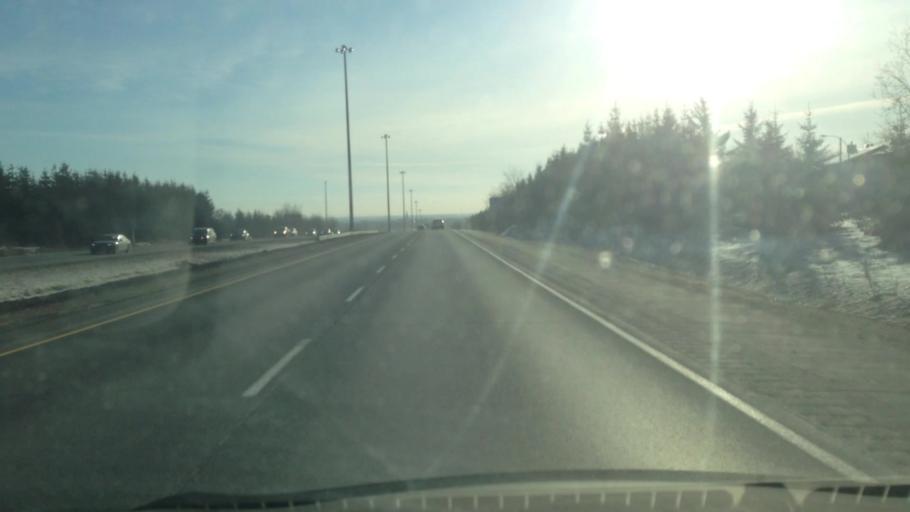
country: CA
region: Quebec
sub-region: Laurentides
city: Saint-Jerome
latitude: 45.8053
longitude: -74.0372
